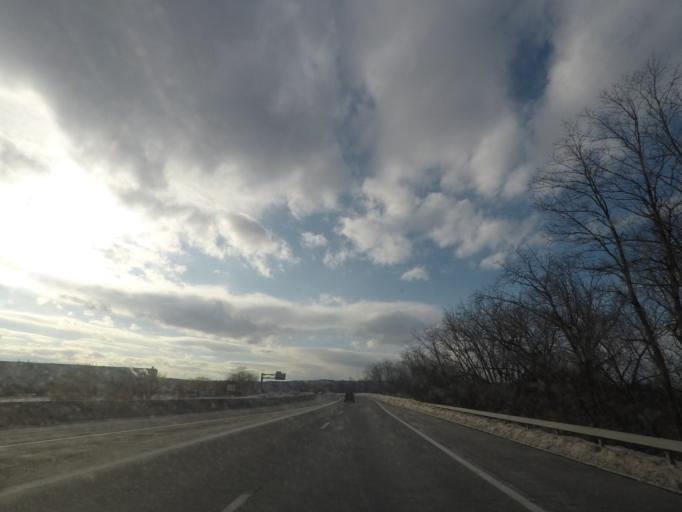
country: US
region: New York
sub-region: Schenectady County
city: Scotia
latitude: 42.8148
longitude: -73.9582
